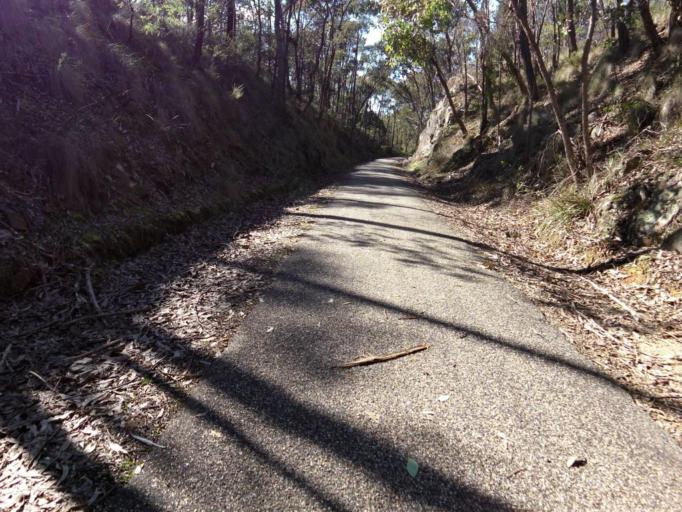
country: AU
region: Victoria
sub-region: Wangaratta
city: Wangaratta
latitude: -36.4033
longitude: 146.6356
